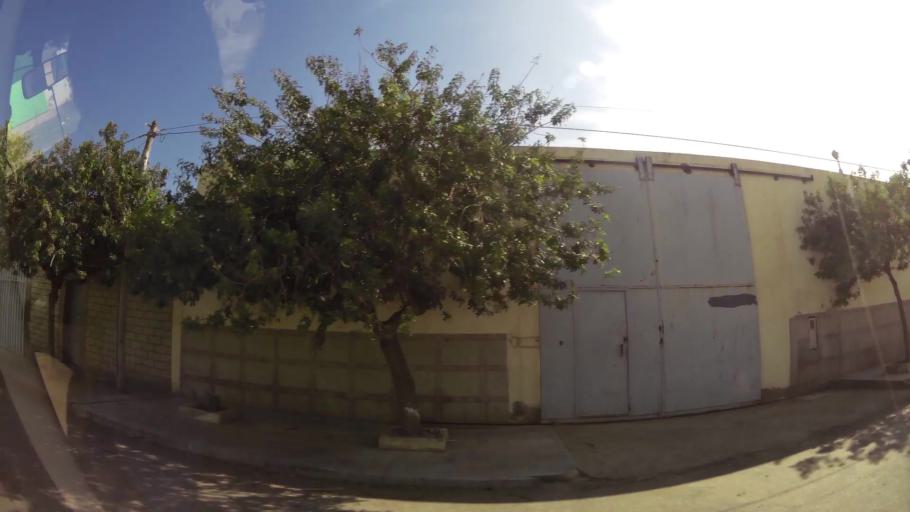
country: MA
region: Oriental
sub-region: Oujda-Angad
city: Oujda
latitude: 34.7092
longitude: -1.8875
